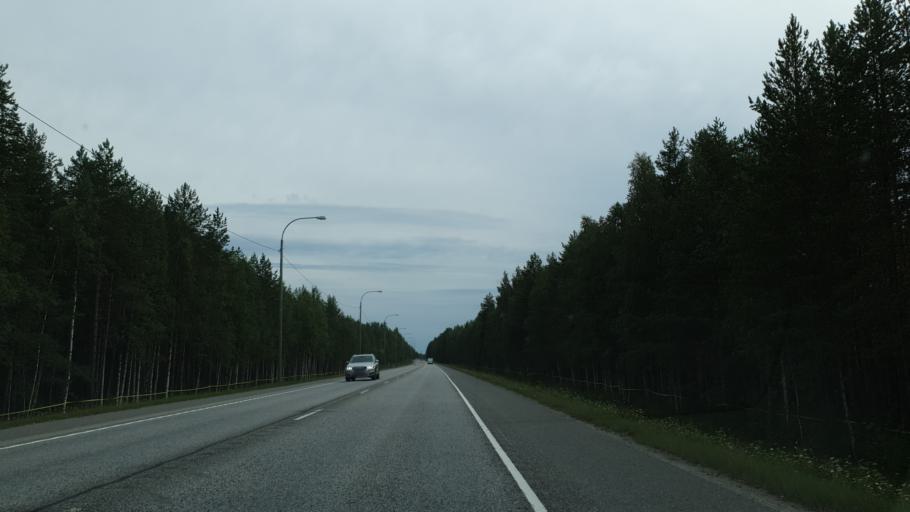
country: FI
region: North Karelia
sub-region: Joensuu
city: Joensuu
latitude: 62.6527
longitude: 29.7845
